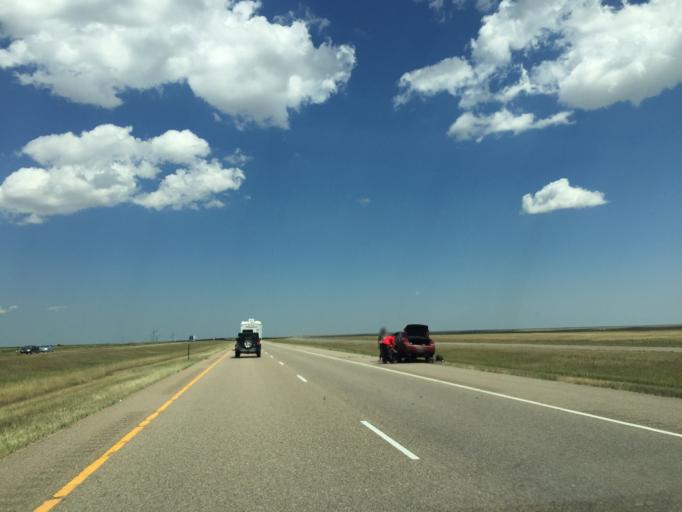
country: US
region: Colorado
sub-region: Lincoln County
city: Hugo
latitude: 39.2769
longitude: -103.4686
